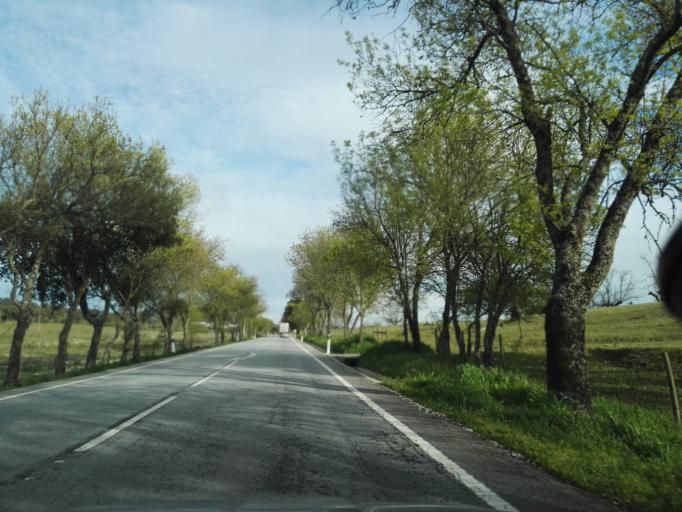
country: PT
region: Portalegre
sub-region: Portalegre
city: Fortios
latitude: 39.3381
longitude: -7.5235
